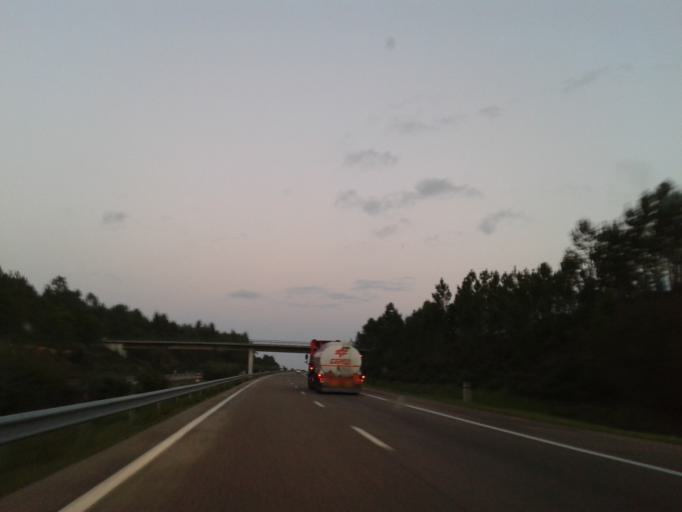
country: PT
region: Evora
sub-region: Vendas Novas
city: Vendas Novas
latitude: 38.6393
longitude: -8.4935
